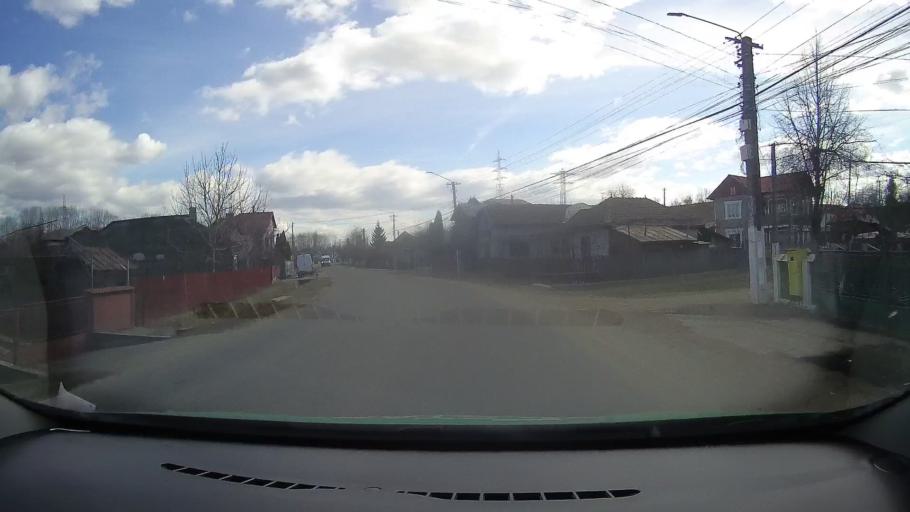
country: RO
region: Dambovita
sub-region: Comuna Doicesti
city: Doicesti
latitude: 44.9744
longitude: 25.3929
